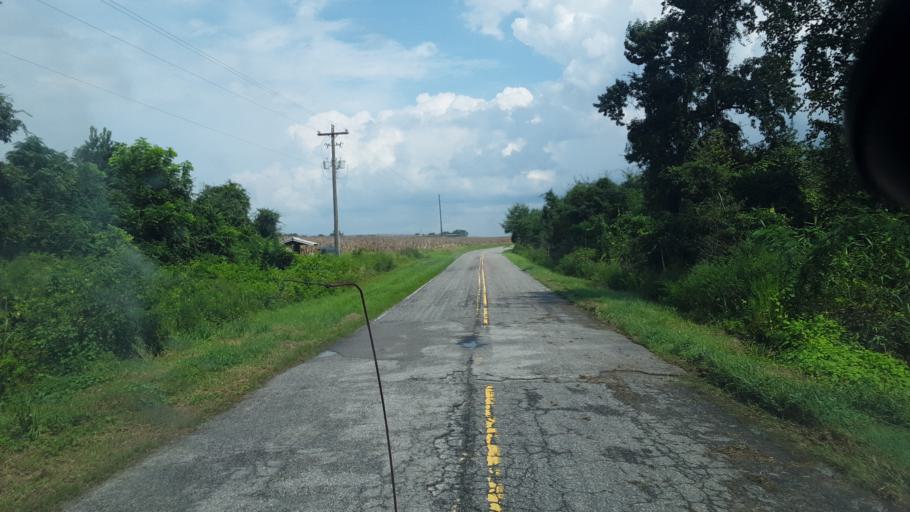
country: US
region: South Carolina
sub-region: Lee County
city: Bishopville
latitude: 34.1782
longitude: -80.1509
